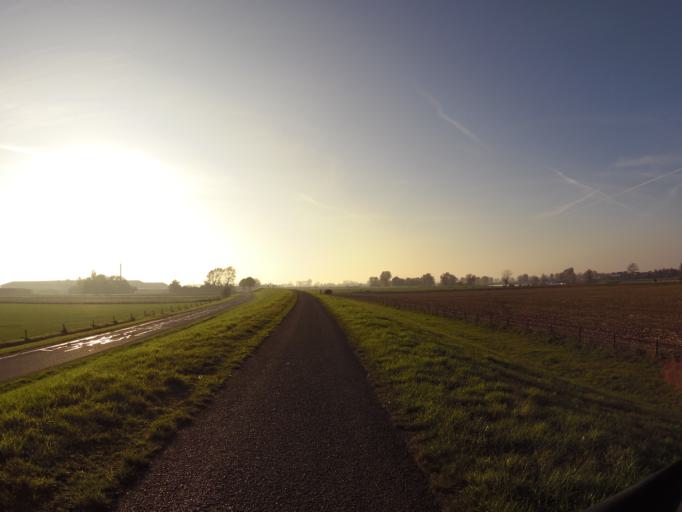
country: NL
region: Gelderland
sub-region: Gemeente Maasdriel
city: Hedel
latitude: 51.7402
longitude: 5.2150
